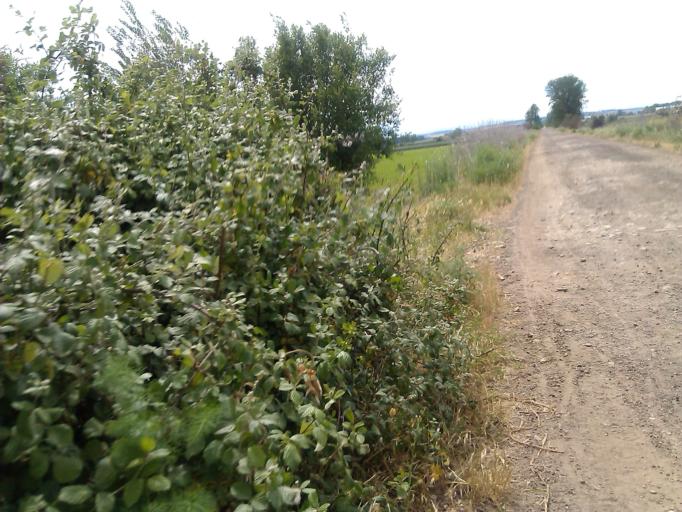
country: ES
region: Castille and Leon
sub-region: Provincia de Leon
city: Hospital de Orbigo
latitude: 42.4597
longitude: -5.8461
